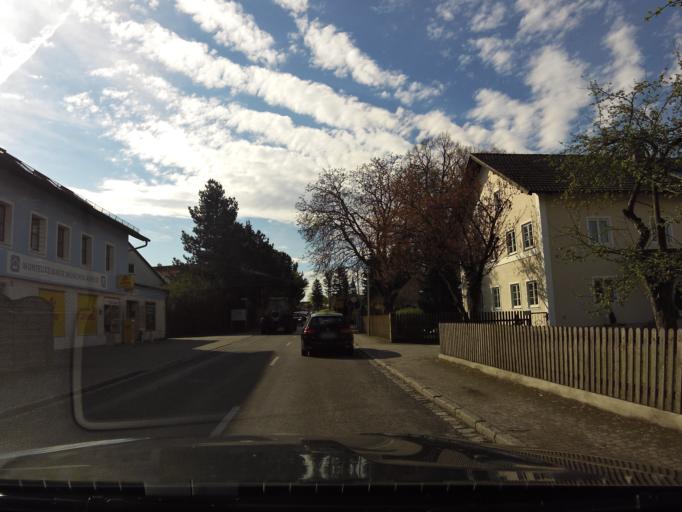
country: DE
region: Bavaria
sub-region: Upper Bavaria
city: Oberding
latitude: 48.3385
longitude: 11.8397
